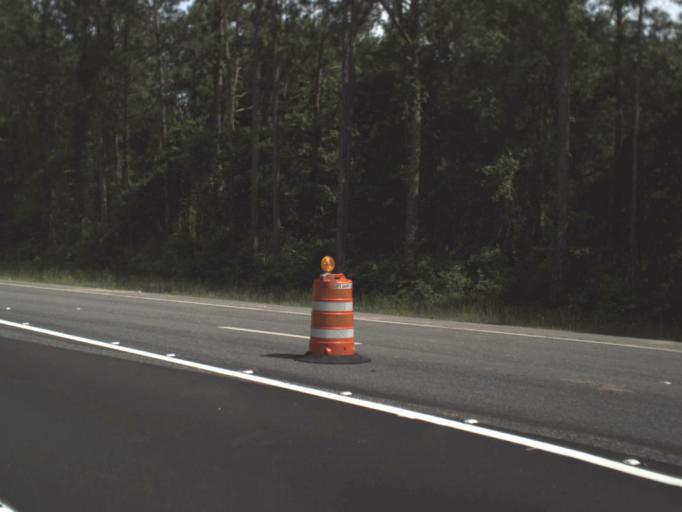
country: US
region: Florida
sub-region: Columbia County
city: Five Points
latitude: 30.2446
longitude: -82.6637
